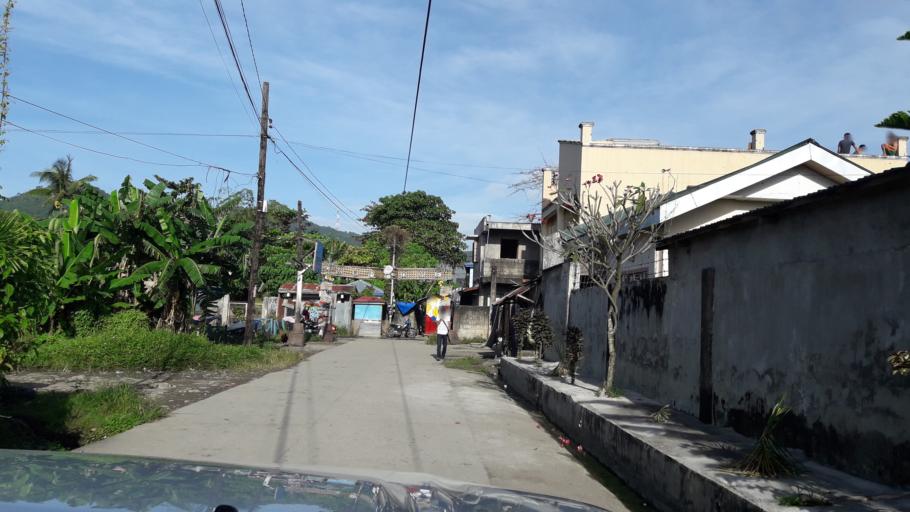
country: PH
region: Eastern Visayas
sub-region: Province of Leyte
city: Panalanoy
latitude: 11.2182
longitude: 125.0011
